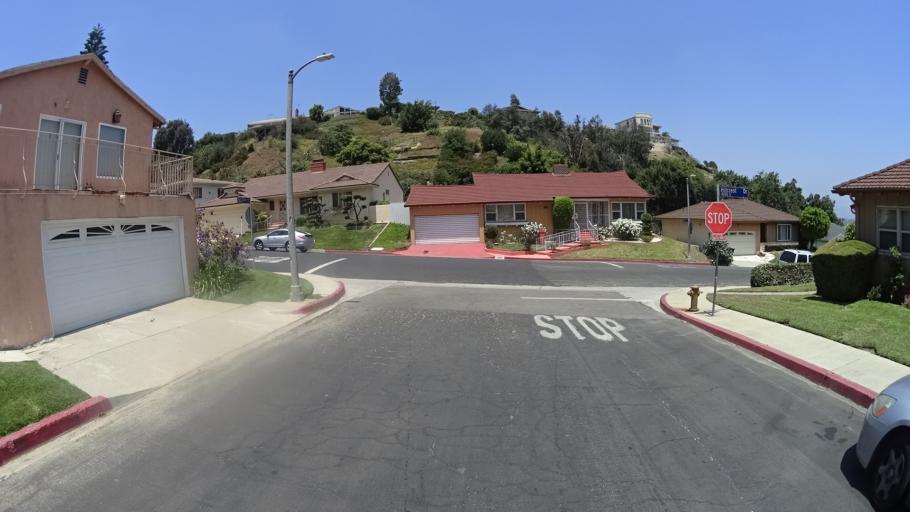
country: US
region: California
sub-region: Los Angeles County
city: View Park-Windsor Hills
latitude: 34.0085
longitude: -118.3510
